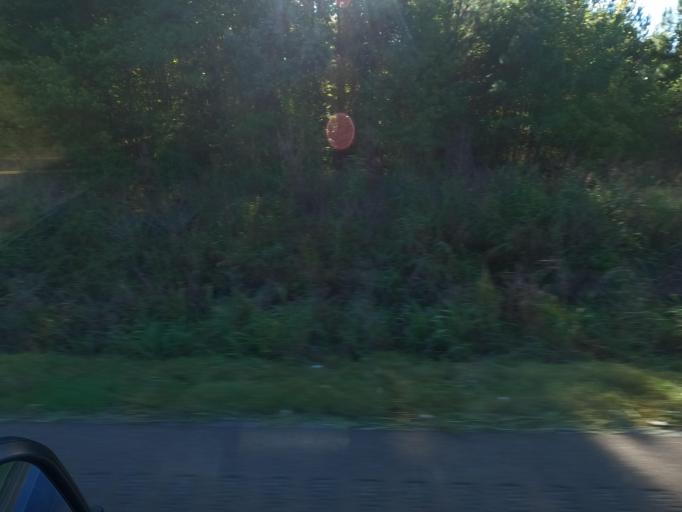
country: US
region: Tennessee
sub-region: Tipton County
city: Brighton
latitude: 35.4695
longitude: -89.7533
